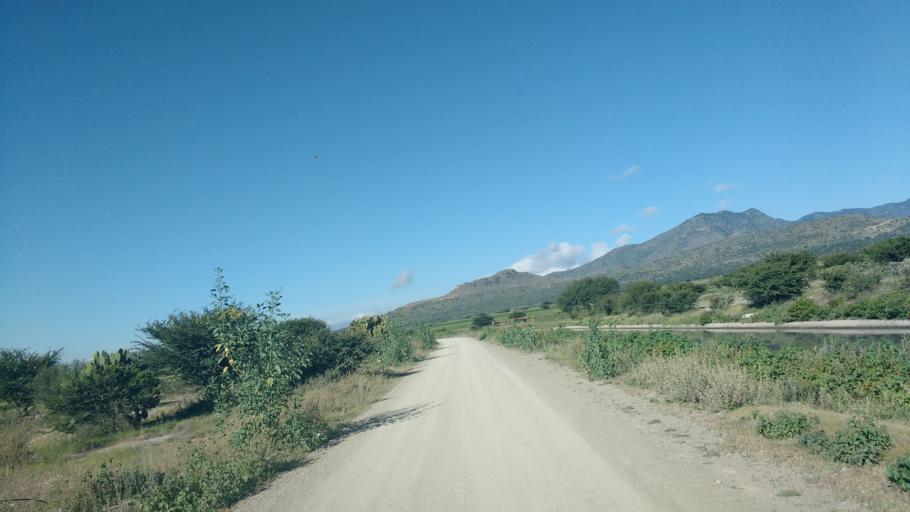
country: MX
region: Hidalgo
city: Mixquiahuala de Juarez
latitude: 20.2539
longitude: -99.2532
